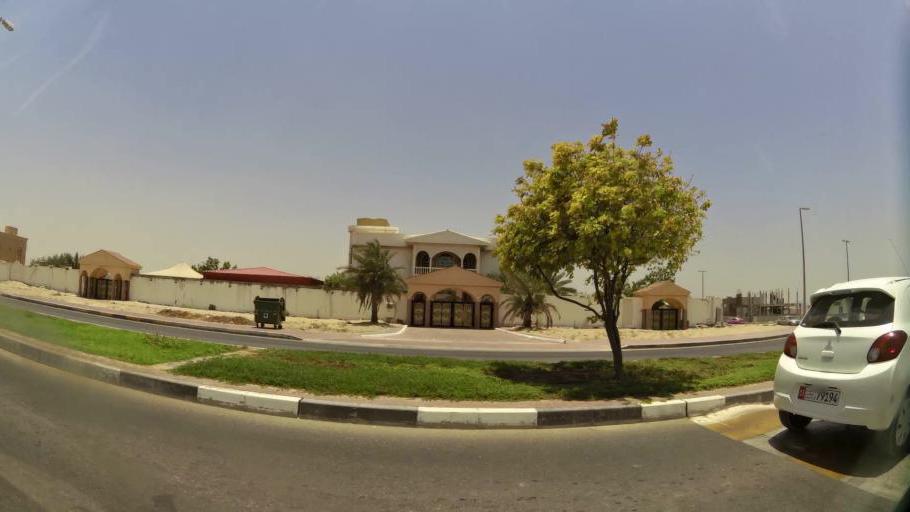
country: AE
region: Ajman
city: Ajman
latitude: 25.4089
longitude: 55.4858
